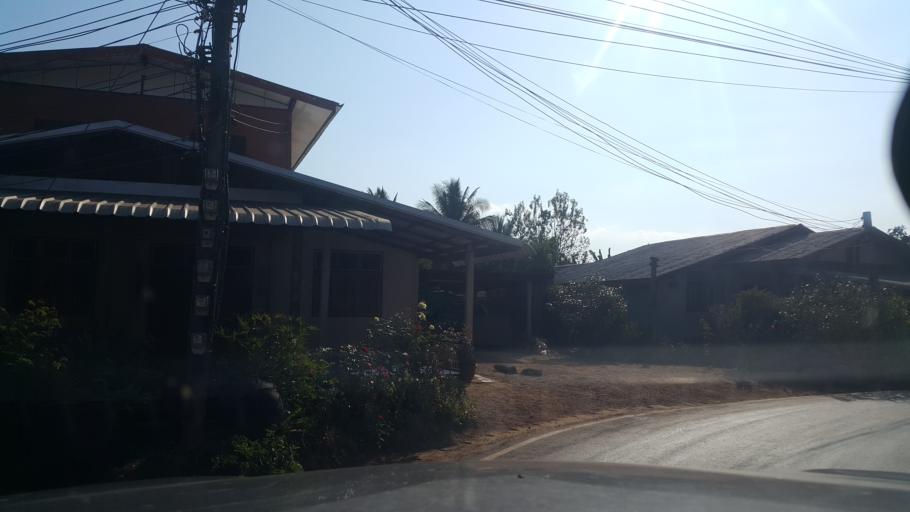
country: TH
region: Loei
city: Chiang Khan
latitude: 17.8045
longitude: 101.6240
